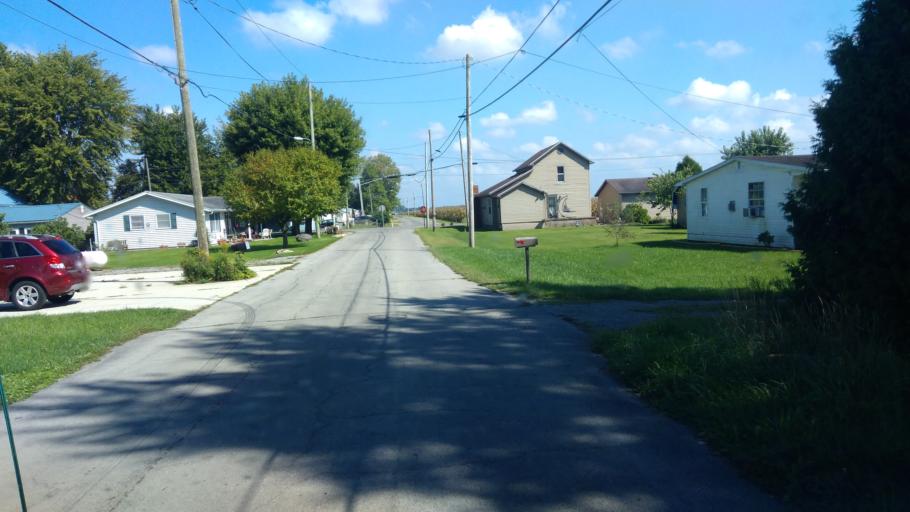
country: US
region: Ohio
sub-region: Hardin County
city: Ada
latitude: 40.7040
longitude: -83.8431
